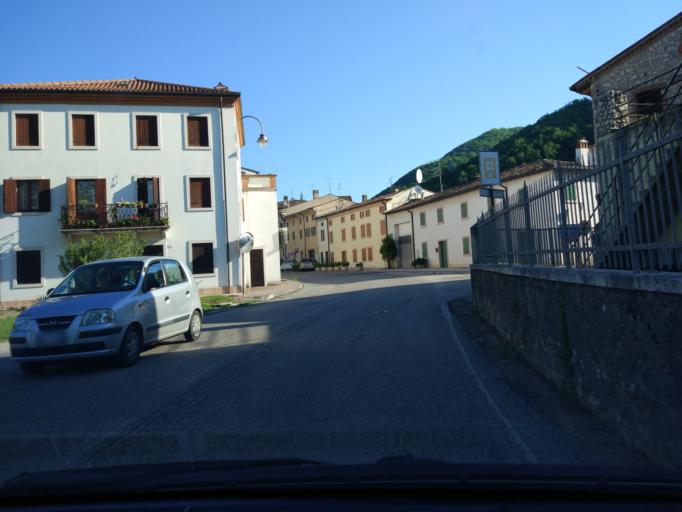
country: IT
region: Veneto
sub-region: Provincia di Verona
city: Badia Calavena
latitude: 45.5623
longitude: 11.1548
